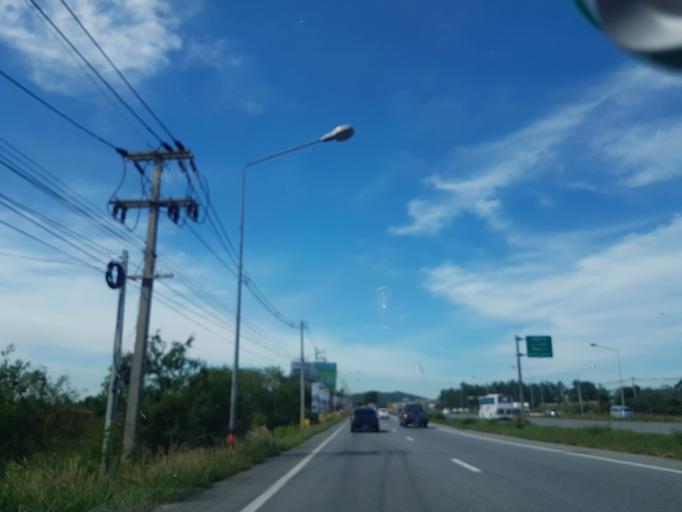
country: TH
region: Chon Buri
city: Phatthaya
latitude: 12.9117
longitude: 101.0259
